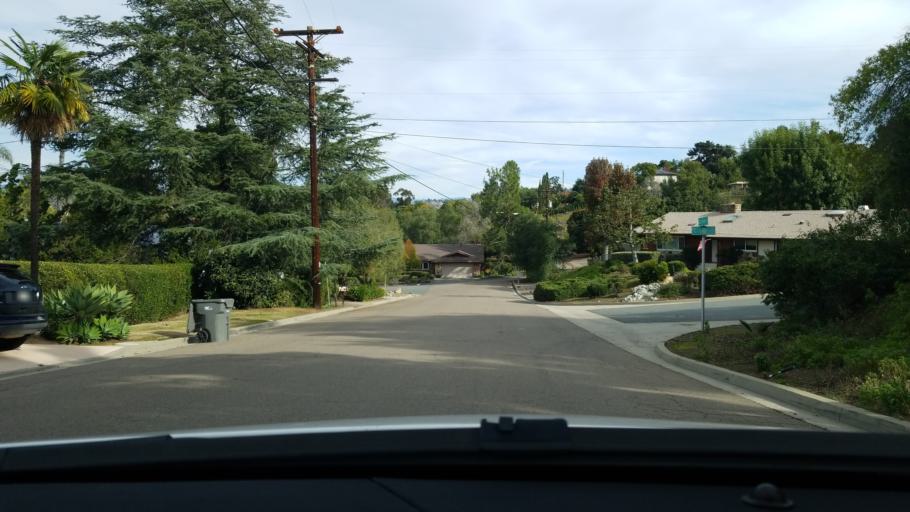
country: US
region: California
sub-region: San Diego County
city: Casa de Oro-Mount Helix
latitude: 32.7717
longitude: -116.9461
